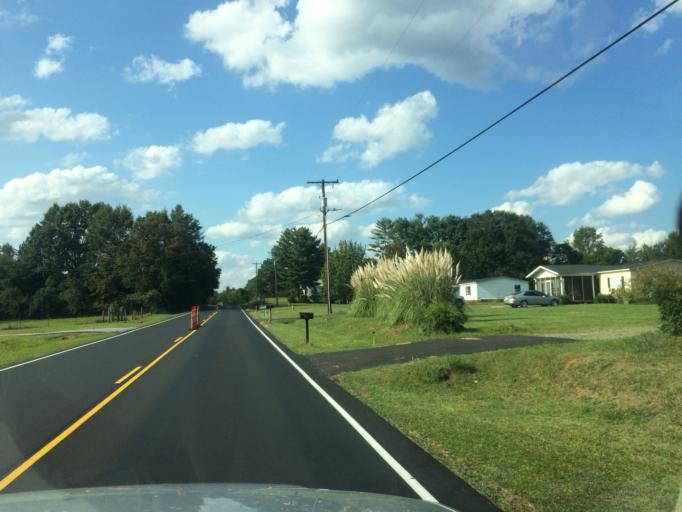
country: US
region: South Carolina
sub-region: Greenwood County
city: Ware Shoals
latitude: 34.4762
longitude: -82.1628
